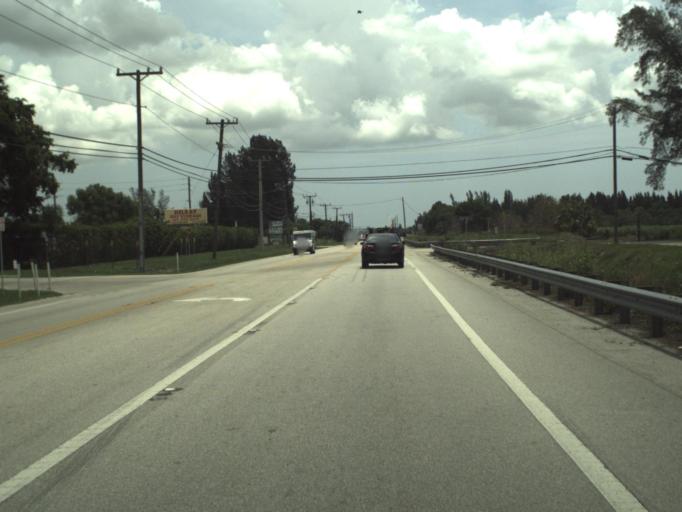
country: US
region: Florida
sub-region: Palm Beach County
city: Villages of Oriole
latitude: 26.4536
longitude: -80.1971
